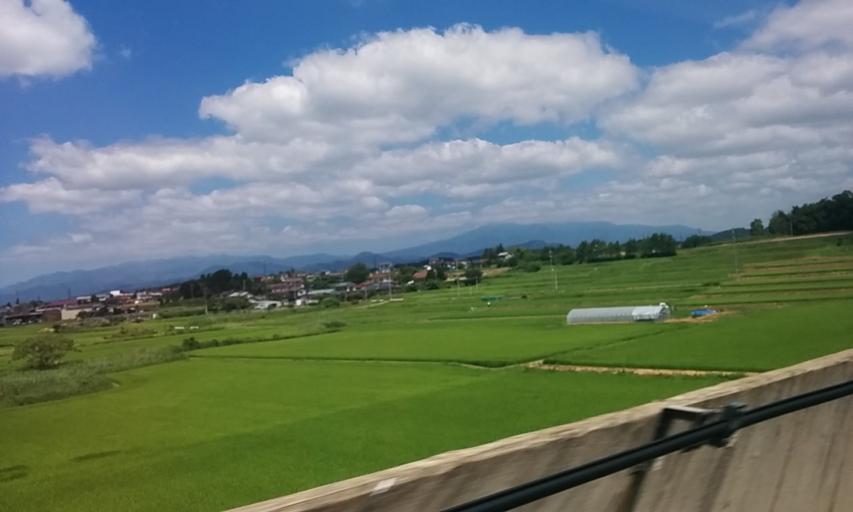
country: JP
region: Fukushima
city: Koriyama
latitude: 37.4428
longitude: 140.4031
